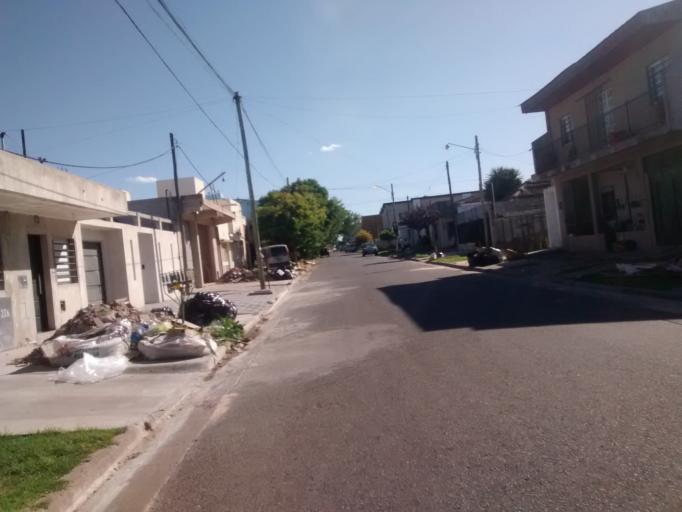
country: AR
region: Buenos Aires
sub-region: Partido de La Plata
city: La Plata
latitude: -34.9269
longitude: -57.9161
